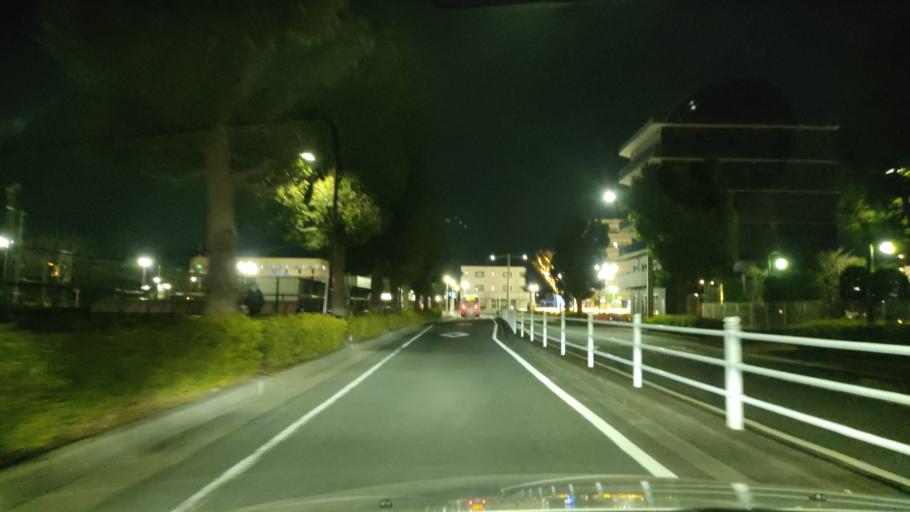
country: JP
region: Chiba
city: Matsudo
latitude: 35.7626
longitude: 139.9132
